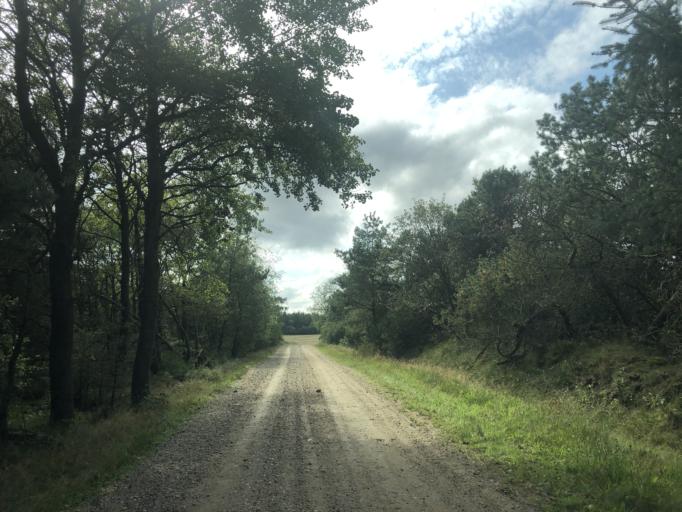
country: DK
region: Central Jutland
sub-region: Holstebro Kommune
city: Ulfborg
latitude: 56.2342
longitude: 8.4451
